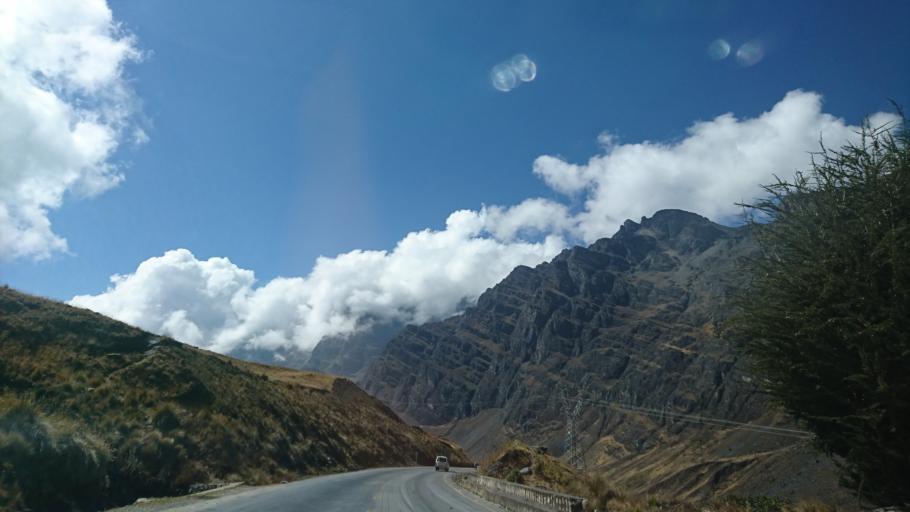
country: BO
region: La Paz
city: La Paz
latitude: -16.3277
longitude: -67.9881
